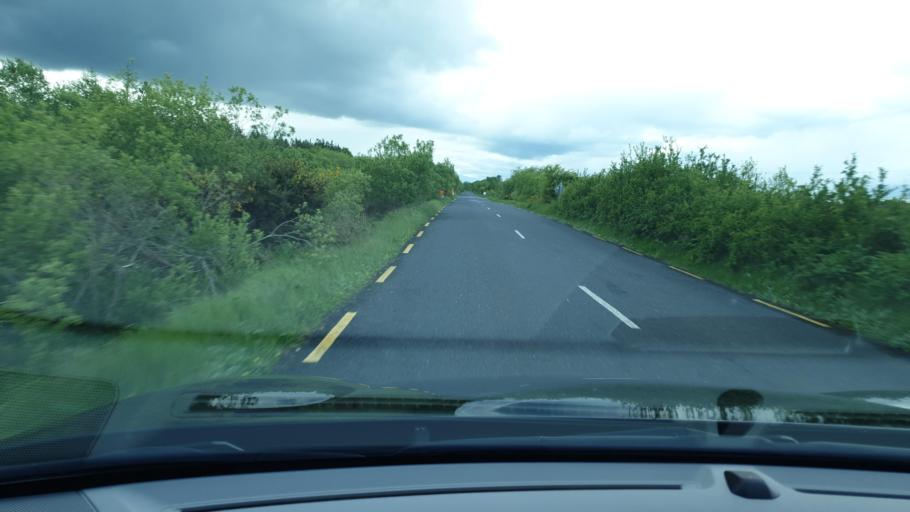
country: IE
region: Leinster
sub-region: Uibh Fhaili
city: Clara
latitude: 53.2380
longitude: -7.6954
